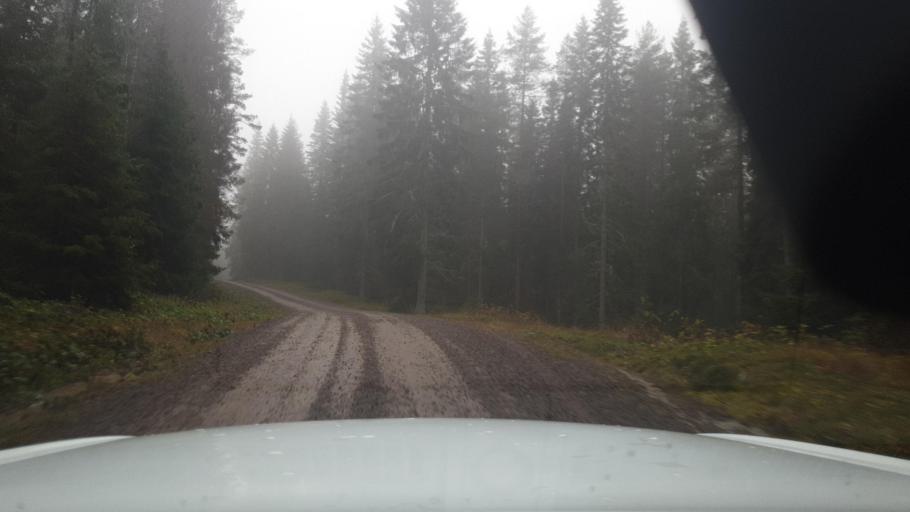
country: SE
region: Vaermland
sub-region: Arvika Kommun
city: Arvika
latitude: 59.9812
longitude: 12.6600
